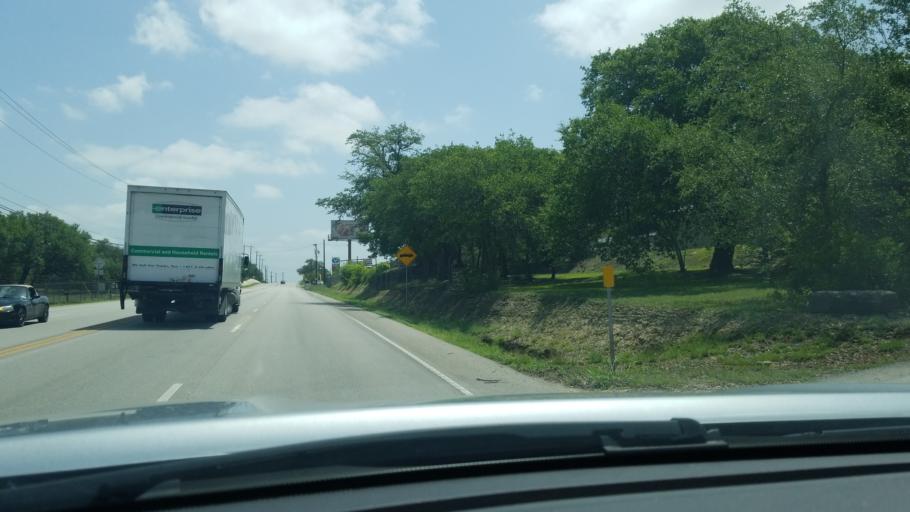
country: US
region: Texas
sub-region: Bexar County
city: Timberwood Park
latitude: 29.7129
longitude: -98.4777
